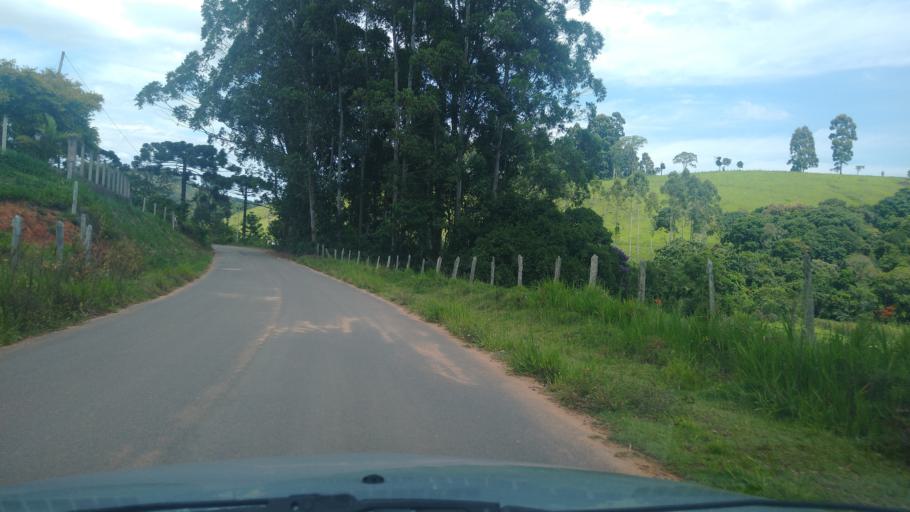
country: BR
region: Minas Gerais
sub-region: Extrema
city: Extrema
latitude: -22.7278
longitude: -46.3110
